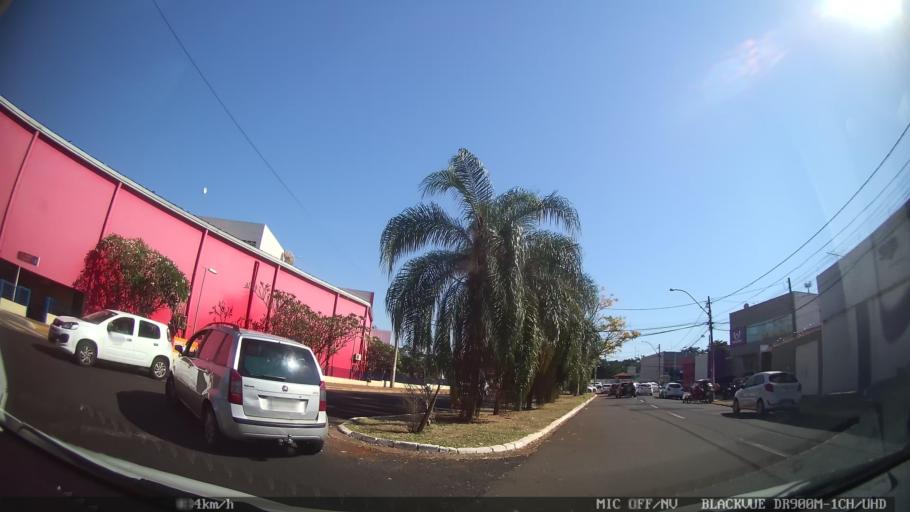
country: BR
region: Sao Paulo
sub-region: Ribeirao Preto
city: Ribeirao Preto
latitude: -21.2028
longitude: -47.8088
